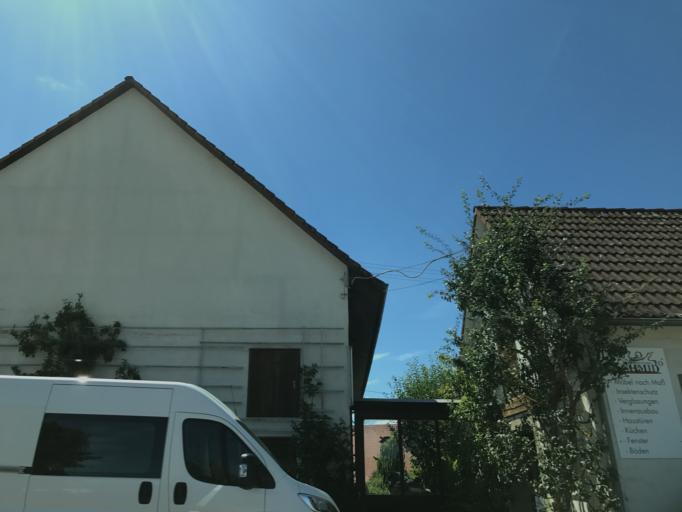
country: DE
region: Baden-Wuerttemberg
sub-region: Tuebingen Region
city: Langenenslingen
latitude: 48.1361
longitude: 9.4049
